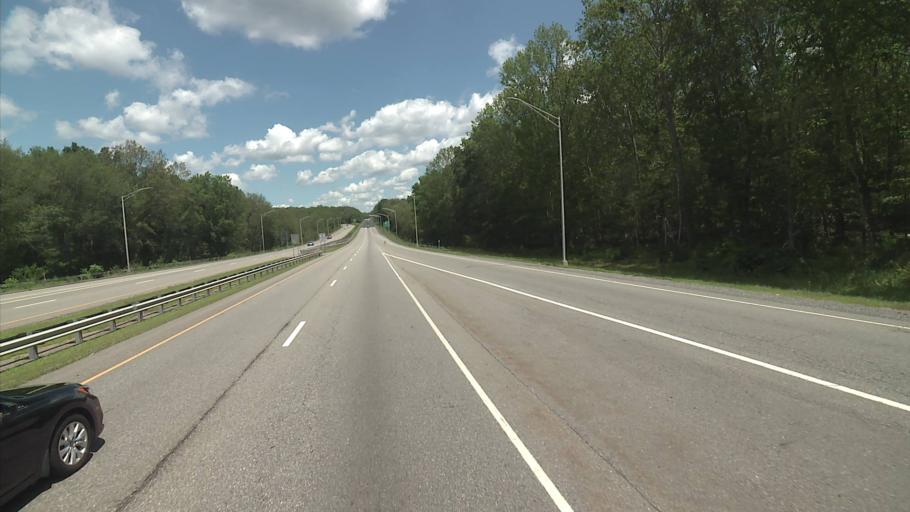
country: US
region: Connecticut
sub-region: Windham County
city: Wauregan
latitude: 41.7554
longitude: -71.8769
